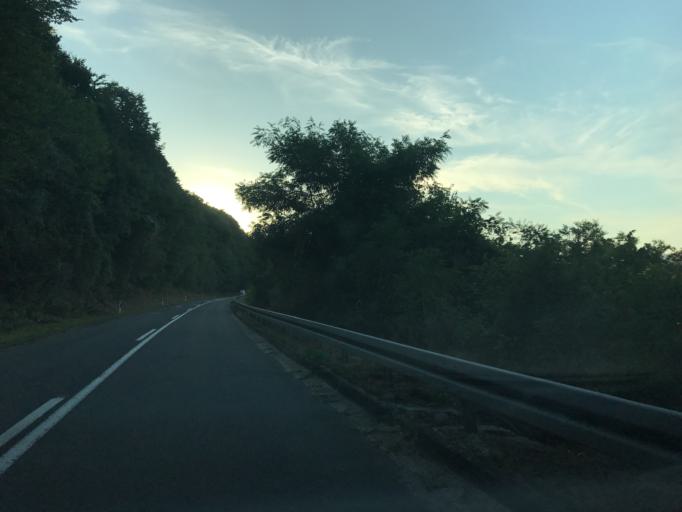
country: RO
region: Caras-Severin
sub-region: Comuna Berzasca
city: Berzasca
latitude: 44.6312
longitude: 21.9515
